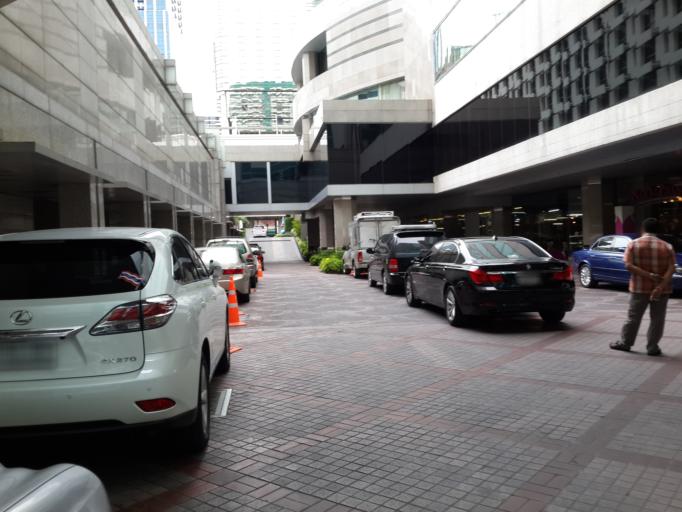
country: TH
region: Bangkok
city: Ratchathewi
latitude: 13.7454
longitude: 100.5418
